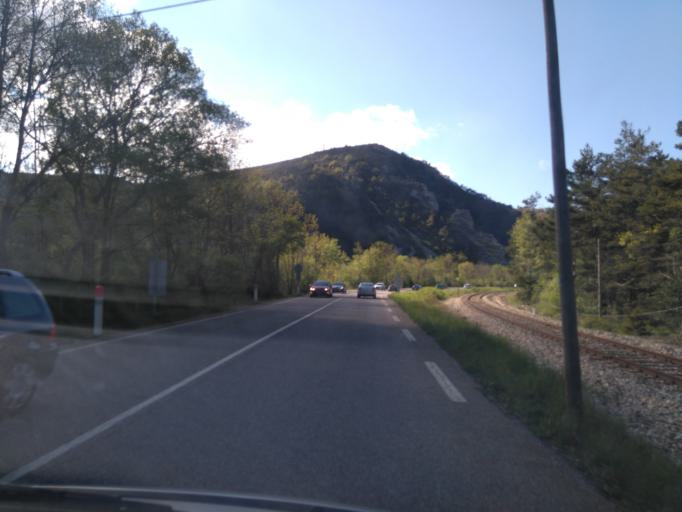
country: FR
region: Provence-Alpes-Cote d'Azur
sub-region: Departement des Hautes-Alpes
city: Veynes
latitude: 44.6205
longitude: 5.7009
